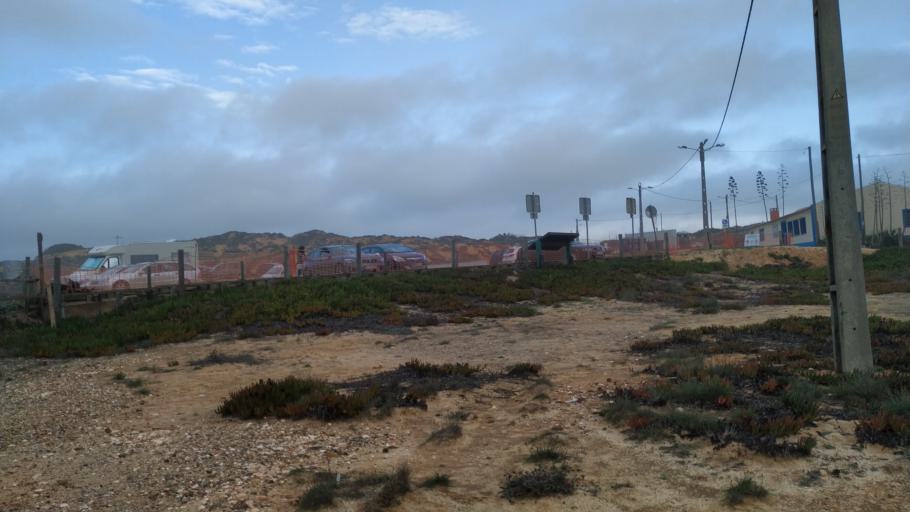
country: PT
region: Beja
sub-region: Odemira
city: Vila Nova de Milfontes
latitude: 37.6533
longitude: -8.8020
